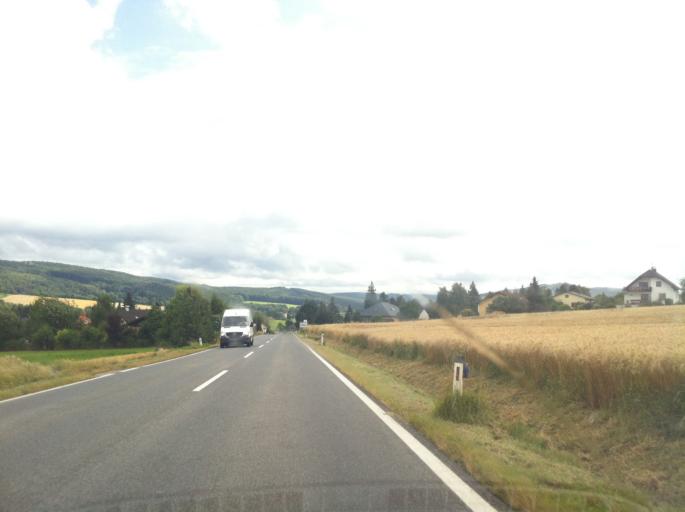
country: AT
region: Lower Austria
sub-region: Politischer Bezirk Tulln
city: Tulbing
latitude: 48.2648
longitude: 16.0760
